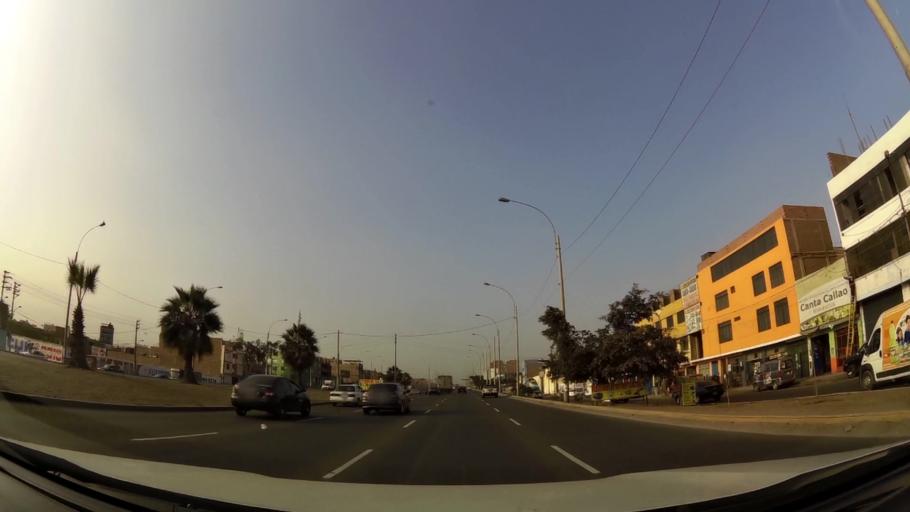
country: PE
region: Lima
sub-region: Lima
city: Independencia
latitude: -11.9832
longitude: -77.0985
